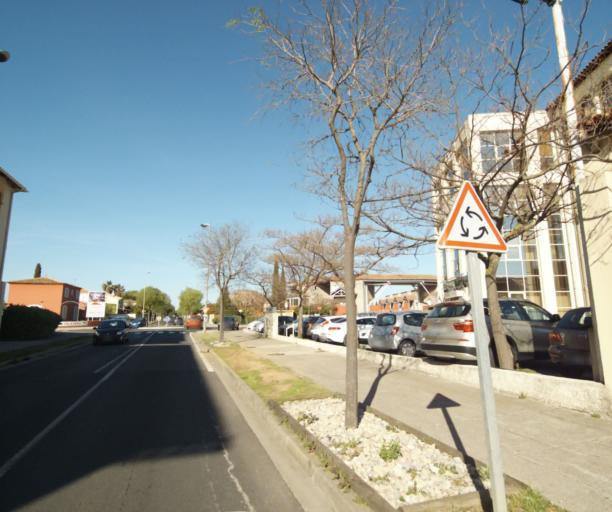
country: FR
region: Languedoc-Roussillon
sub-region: Departement de l'Herault
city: Lattes
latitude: 43.5718
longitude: 3.9067
